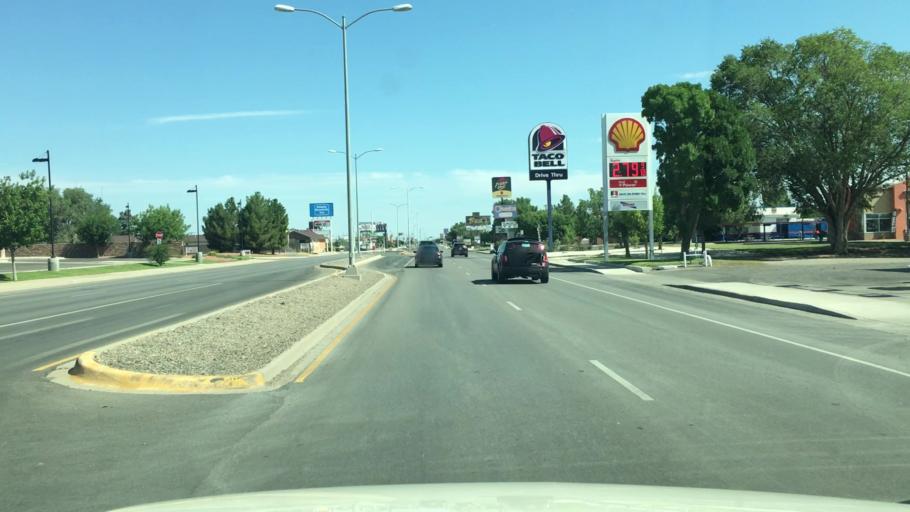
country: US
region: New Mexico
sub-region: Chaves County
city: Roswell
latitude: 33.4323
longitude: -104.5231
